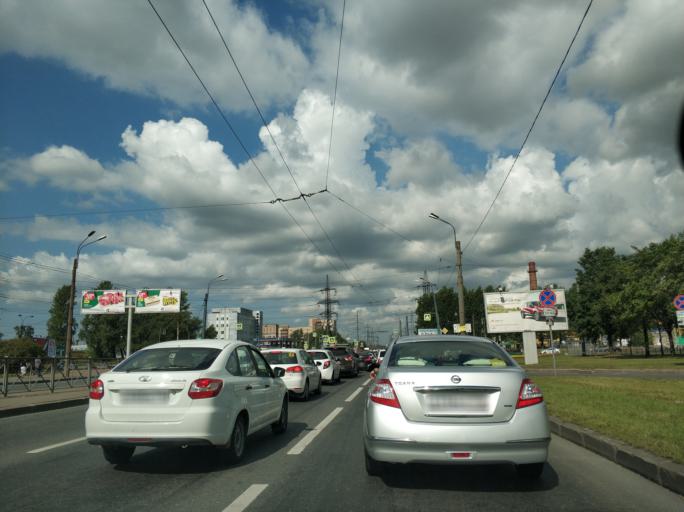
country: RU
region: St.-Petersburg
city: Krasnogvargeisky
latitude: 59.9550
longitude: 30.4680
